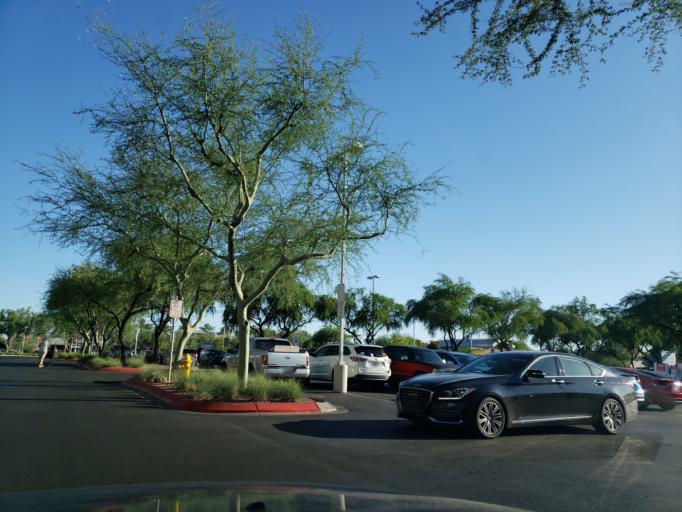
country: US
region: Arizona
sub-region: Maricopa County
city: Paradise Valley
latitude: 33.6789
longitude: -111.9752
